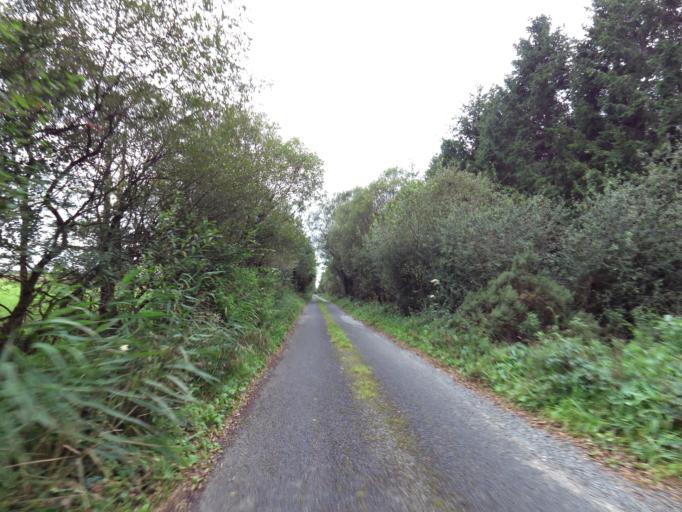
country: IE
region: Leinster
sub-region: Uibh Fhaili
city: Ferbane
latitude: 53.2471
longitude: -7.7393
